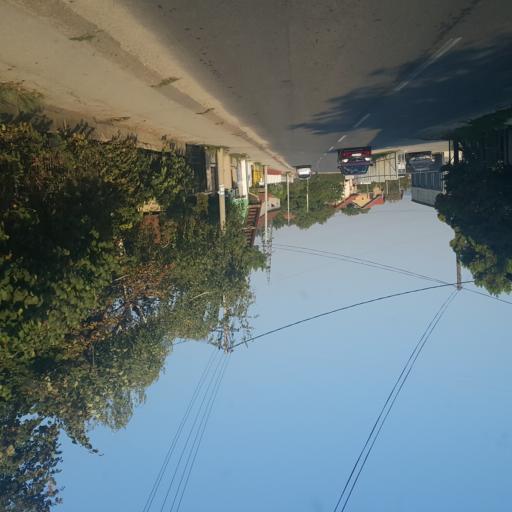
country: RS
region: Central Serbia
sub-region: Zajecarski Okrug
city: Zajecar
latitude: 43.9142
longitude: 22.2817
